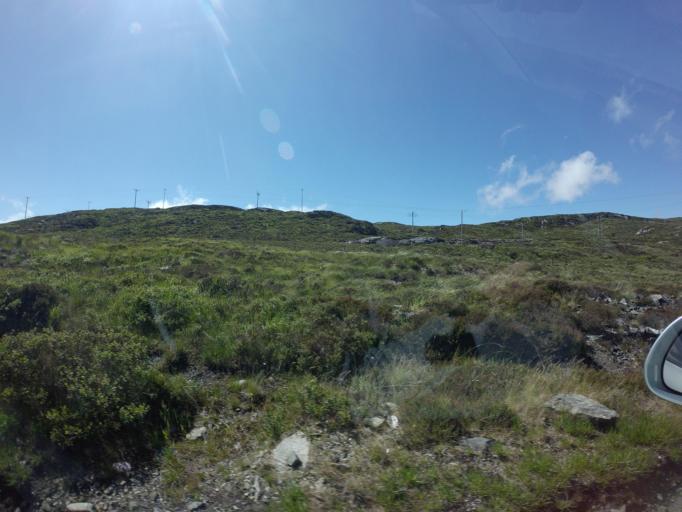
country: GB
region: Scotland
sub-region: Eilean Siar
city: Stornoway
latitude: 58.1339
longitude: -6.5071
